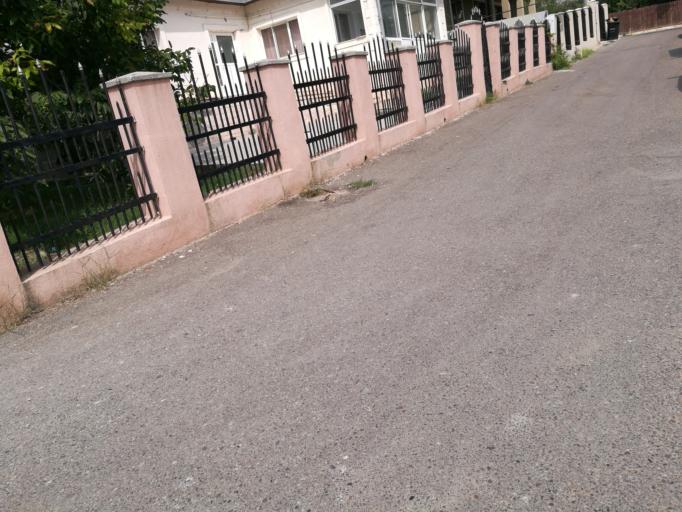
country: RO
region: Iasi
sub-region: Comuna Miroslava
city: Miroslava
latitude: 47.1737
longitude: 27.5314
